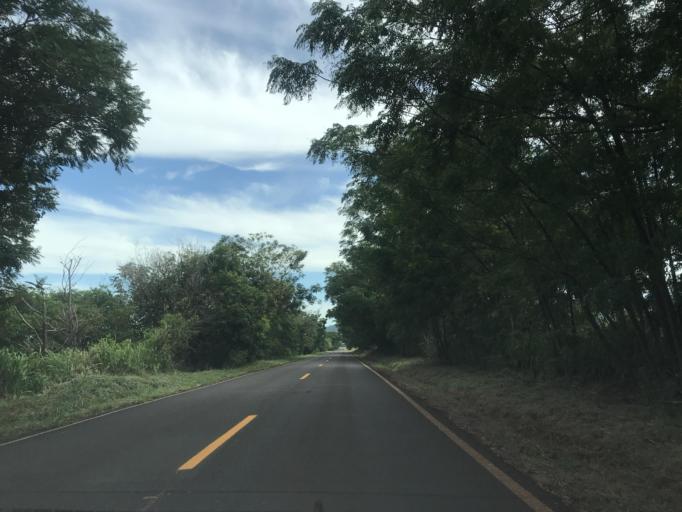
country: BR
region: Parana
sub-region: Paranavai
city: Nova Aurora
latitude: -22.8134
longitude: -52.6545
